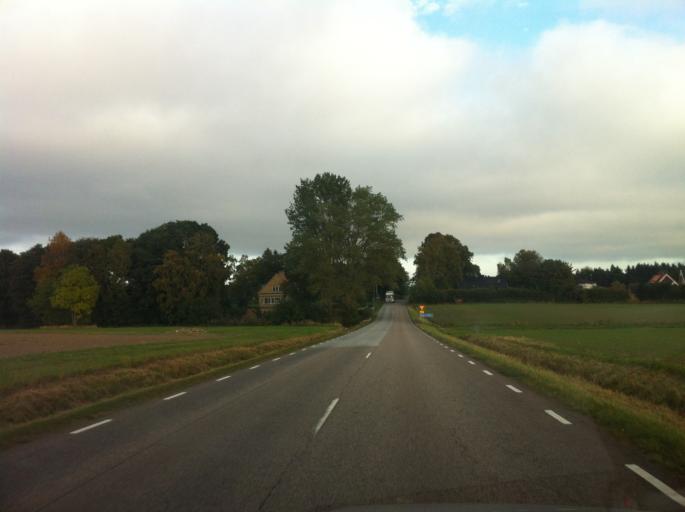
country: SE
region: Skane
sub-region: Helsingborg
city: Morarp
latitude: 56.0578
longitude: 12.8197
